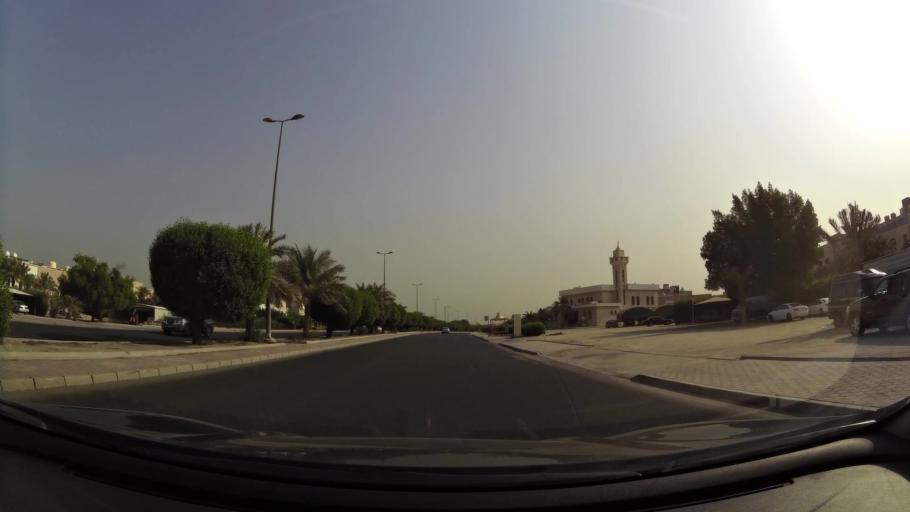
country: KW
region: Mubarak al Kabir
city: Sabah as Salim
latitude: 29.2467
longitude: 48.0691
